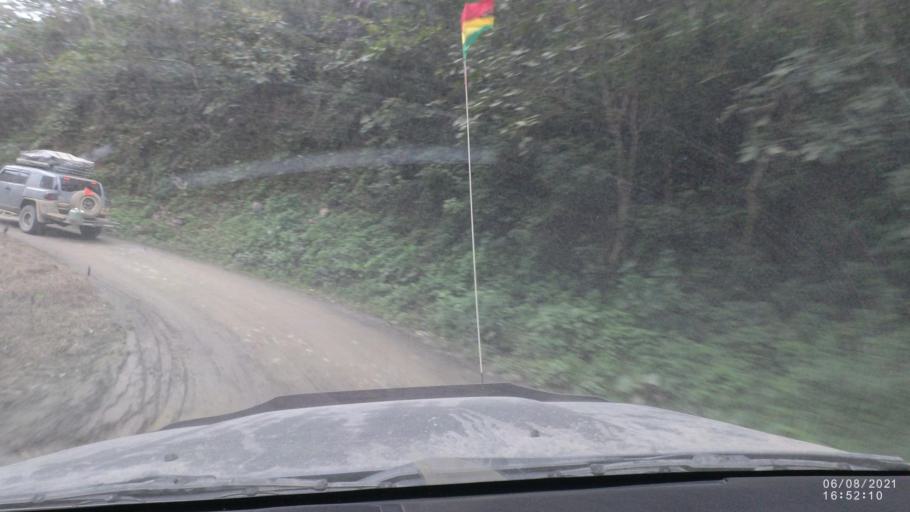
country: BO
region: La Paz
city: Quime
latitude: -16.4941
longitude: -66.7764
